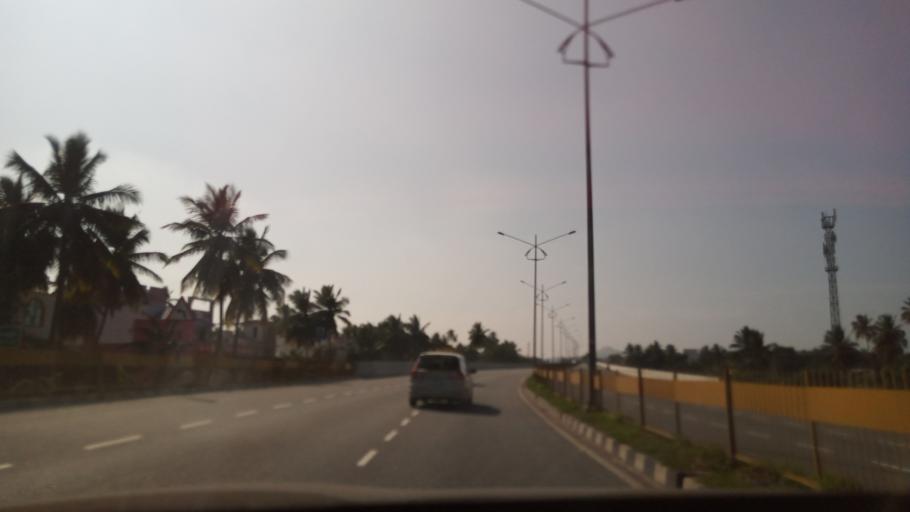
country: IN
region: Tamil Nadu
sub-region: Vellore
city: Jolarpettai
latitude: 12.5485
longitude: 78.4419
